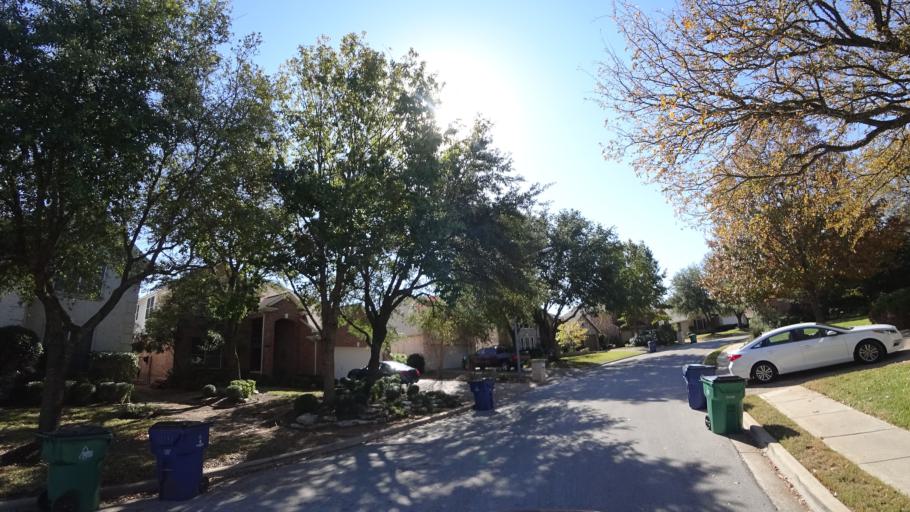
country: US
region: Texas
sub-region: Travis County
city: Lost Creek
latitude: 30.3757
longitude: -97.8441
